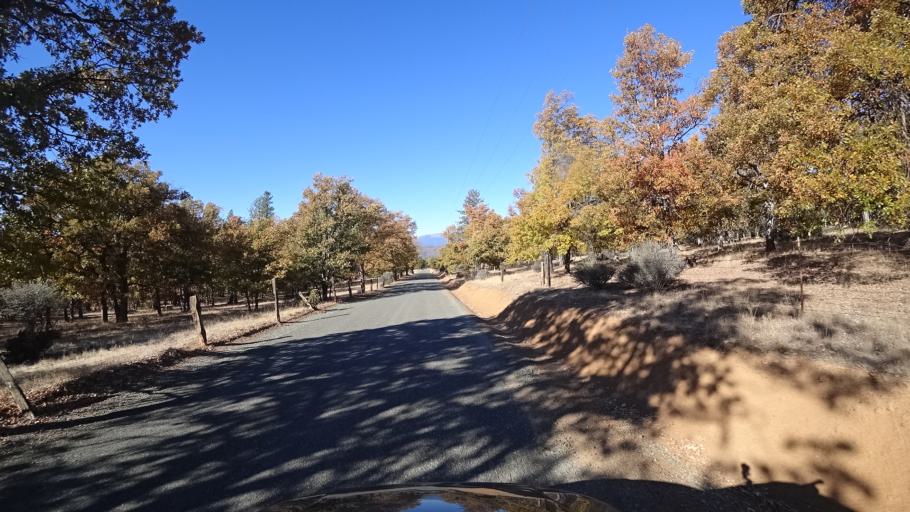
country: US
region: California
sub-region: Siskiyou County
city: Yreka
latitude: 41.5776
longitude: -122.8121
